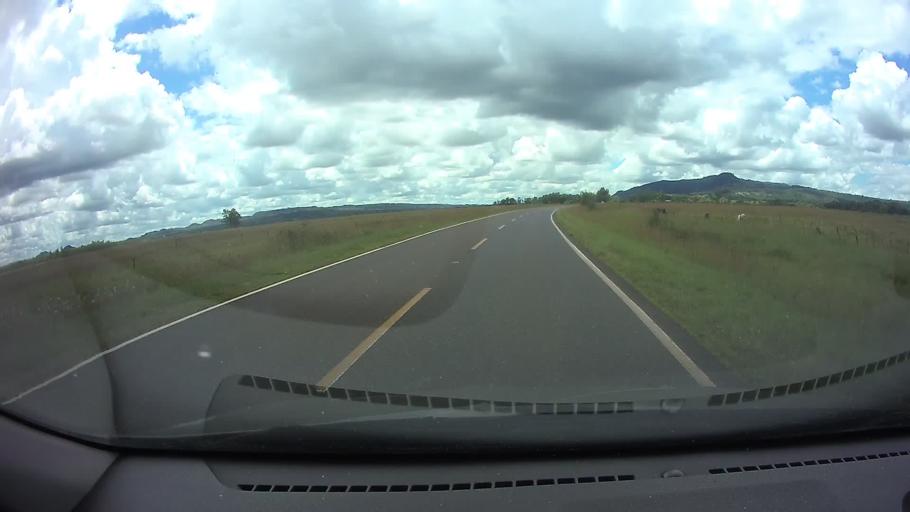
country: PY
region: Paraguari
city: Ybycui
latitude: -25.9098
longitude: -57.0151
